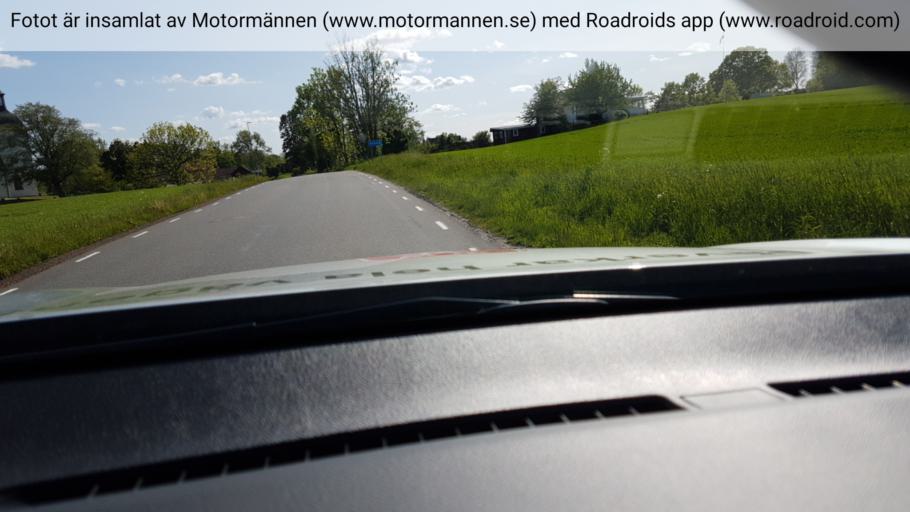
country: SE
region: Vaestra Goetaland
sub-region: Skara Kommun
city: Axvall
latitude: 58.4095
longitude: 13.6055
